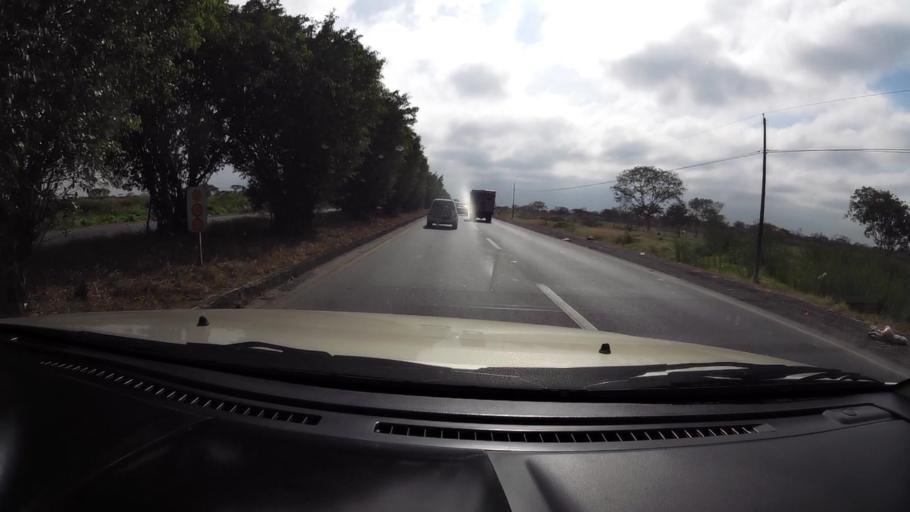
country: EC
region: Guayas
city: Eloy Alfaro
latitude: -2.1992
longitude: -79.7701
